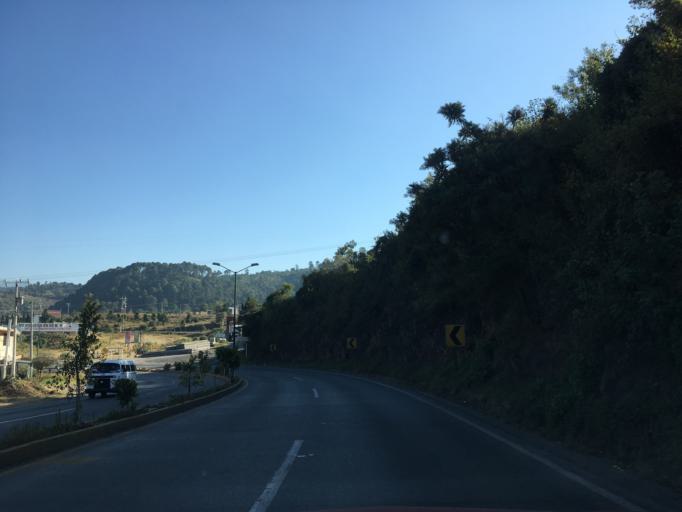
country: MX
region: Michoacan
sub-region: Zitacuaro
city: La Mesa (La Mesa de Cedano)
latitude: 19.4531
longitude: -100.3452
